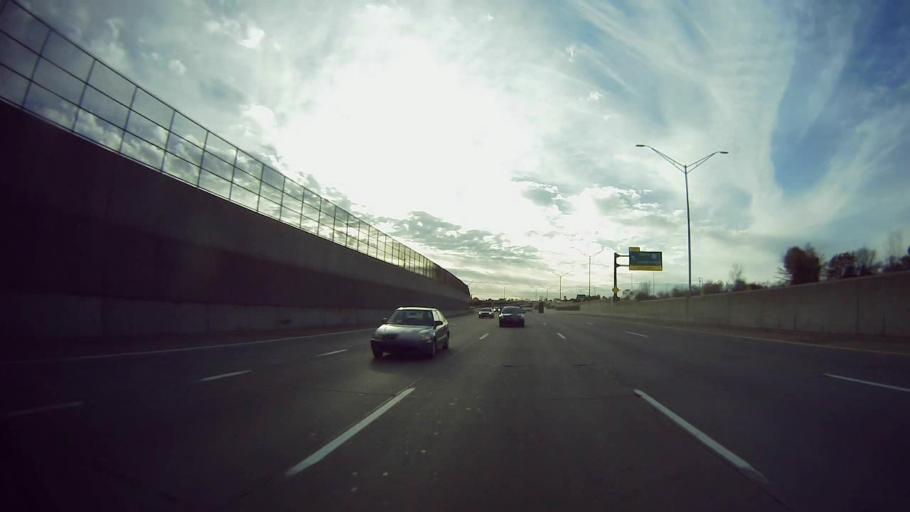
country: US
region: Michigan
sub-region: Wayne County
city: Highland Park
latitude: 42.3998
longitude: -83.1052
